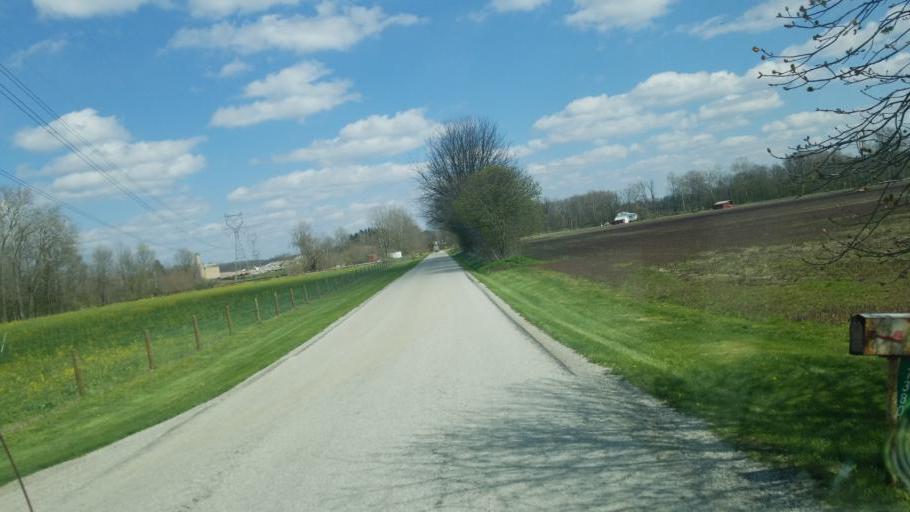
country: US
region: Ohio
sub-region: Licking County
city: Beechwood Trails
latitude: 40.0946
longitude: -82.6329
